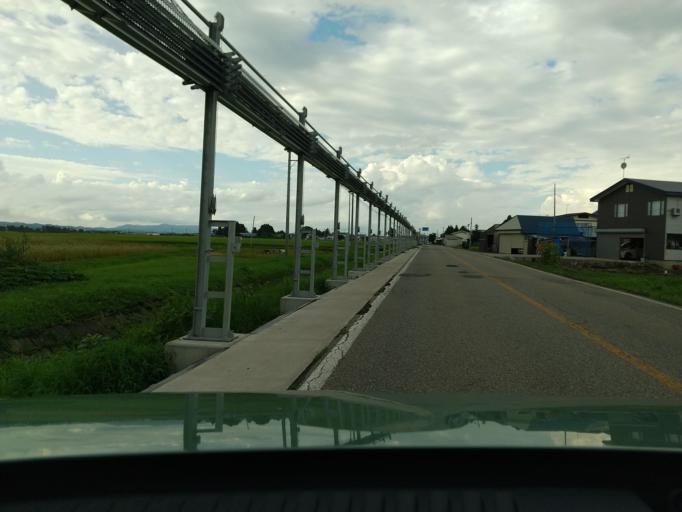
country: JP
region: Akita
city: Yokotemachi
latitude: 39.3142
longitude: 140.4896
